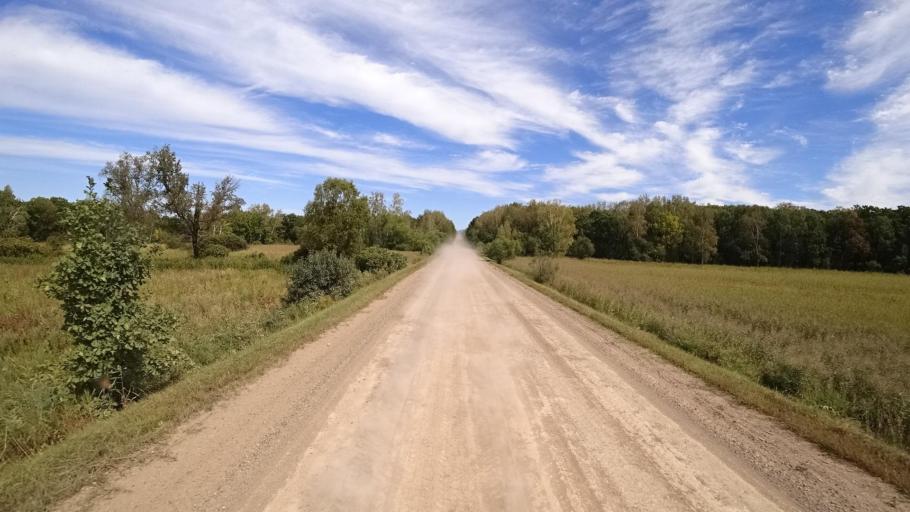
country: RU
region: Primorskiy
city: Yakovlevka
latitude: 44.6984
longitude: 133.6265
